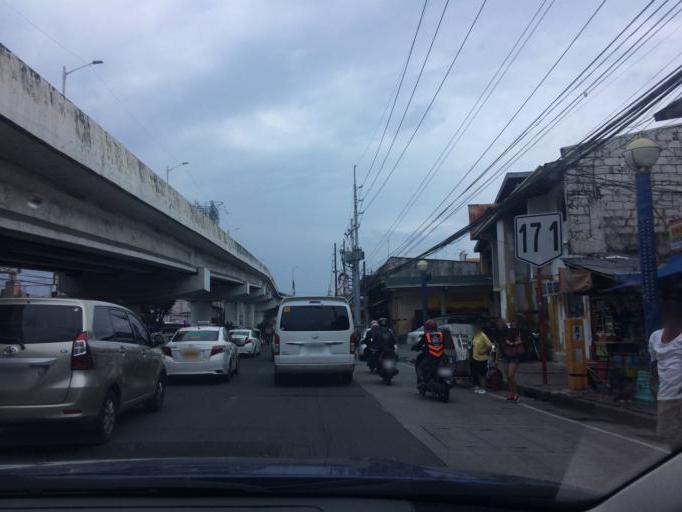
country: PH
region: Metro Manila
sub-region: Makati City
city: Makati City
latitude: 14.5361
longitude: 121.0034
